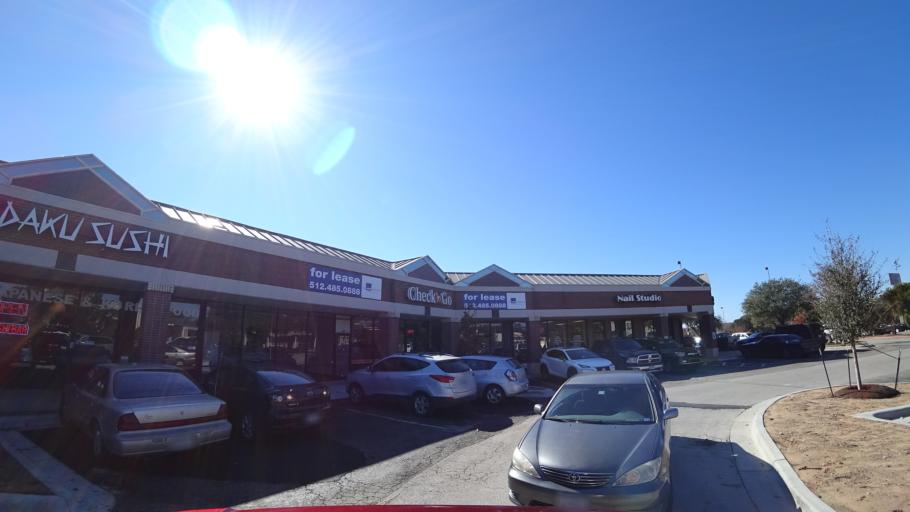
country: US
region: Texas
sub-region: Travis County
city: Wells Branch
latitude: 30.4182
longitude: -97.7024
